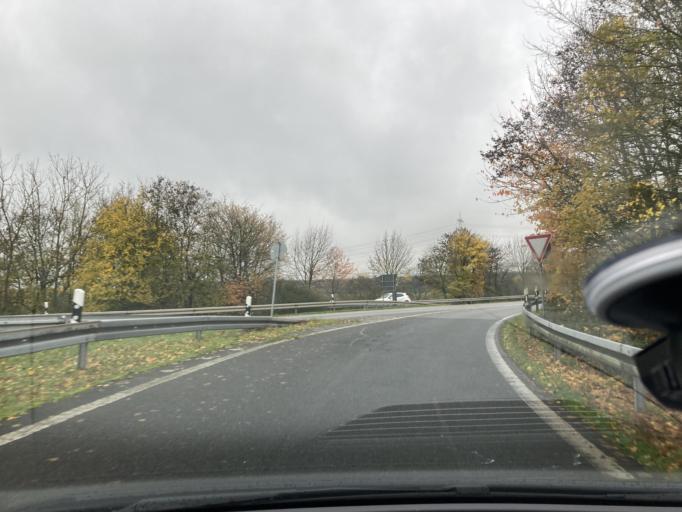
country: DE
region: Hesse
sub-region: Regierungsbezirk Darmstadt
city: Russelsheim
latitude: 49.9667
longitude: 8.3959
